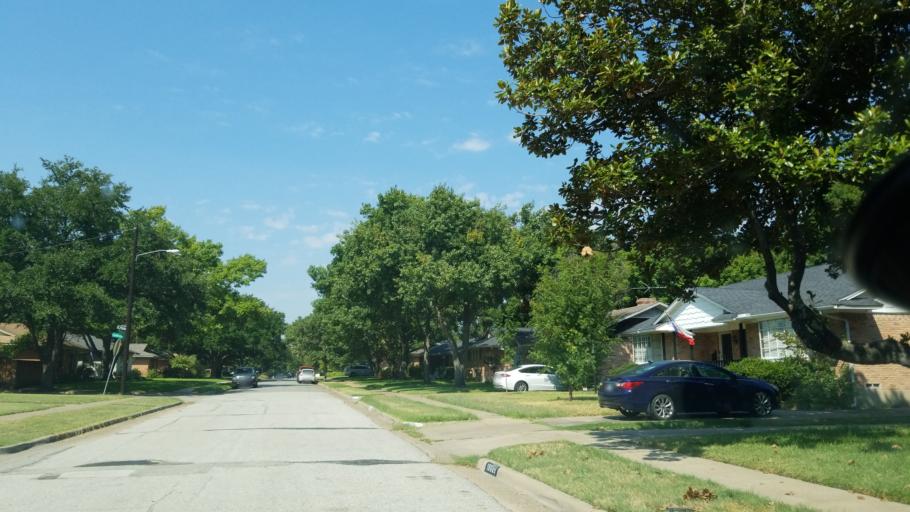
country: US
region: Texas
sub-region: Dallas County
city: Garland
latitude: 32.8759
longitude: -96.7029
